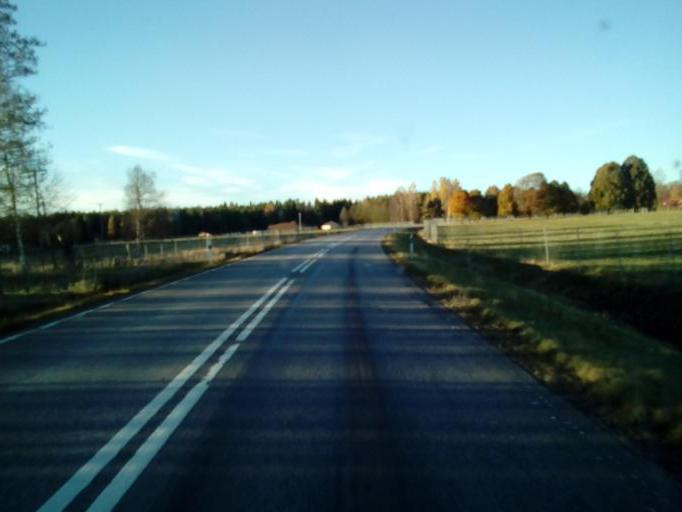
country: SE
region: OErebro
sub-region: Hallsbergs Kommun
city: Palsboda
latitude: 58.9460
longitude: 15.4195
